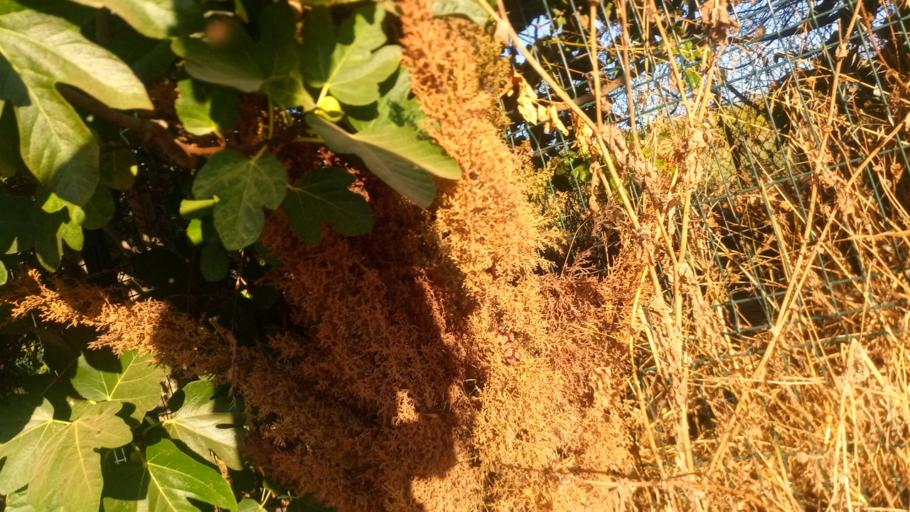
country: PT
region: Faro
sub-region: Tavira
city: Tavira
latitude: 37.1448
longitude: -7.5830
